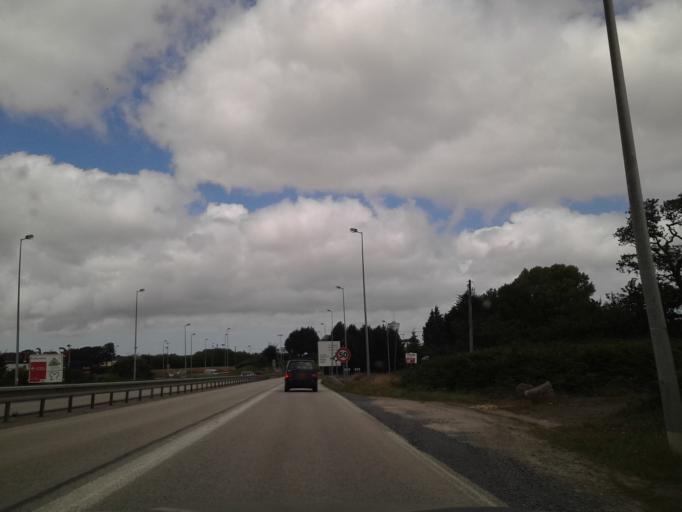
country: FR
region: Lower Normandy
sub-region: Departement de la Manche
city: La Glacerie
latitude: 49.5973
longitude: -1.5965
